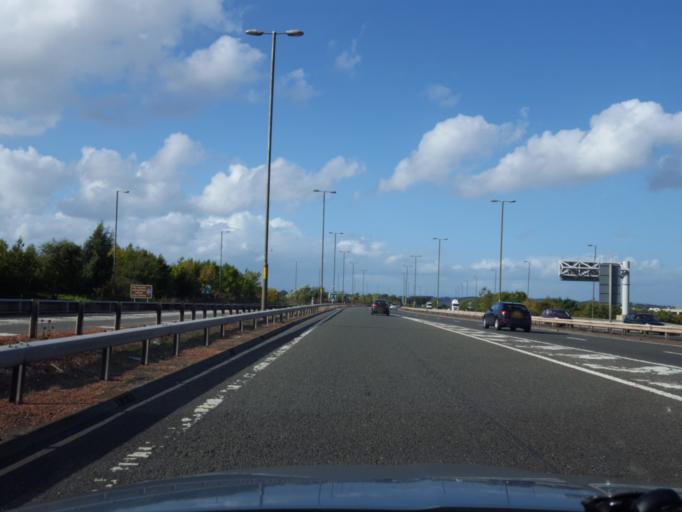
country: GB
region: Scotland
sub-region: Edinburgh
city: Currie
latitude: 55.9271
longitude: -3.3154
